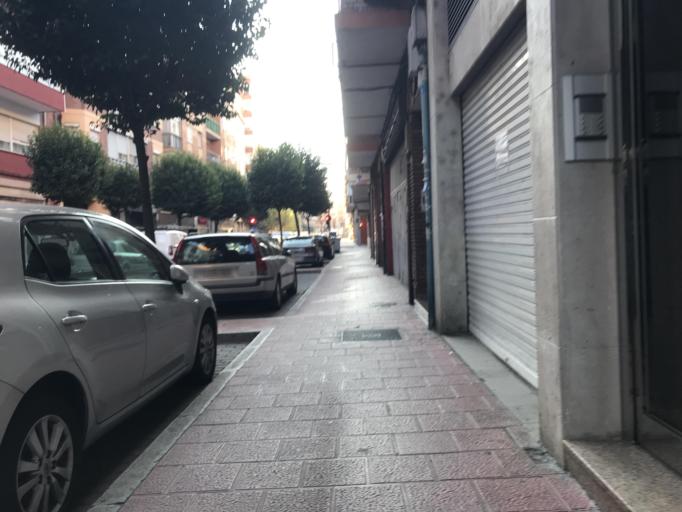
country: ES
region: Castille and Leon
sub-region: Provincia de Valladolid
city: Valladolid
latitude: 41.6512
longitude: -4.7166
